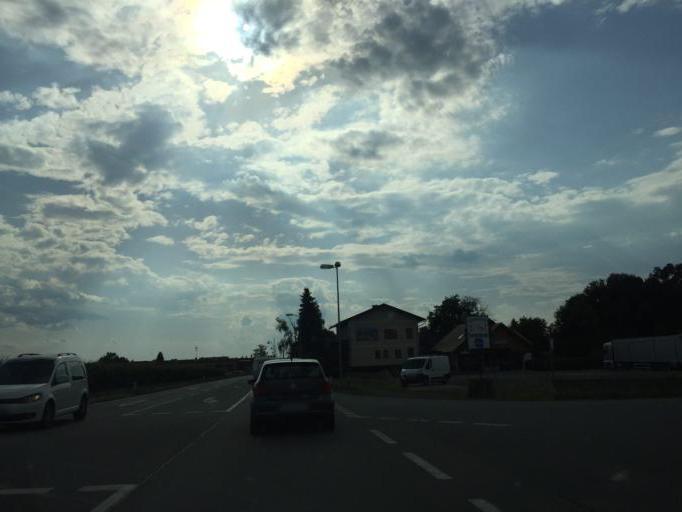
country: AT
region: Styria
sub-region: Politischer Bezirk Suedoststeiermark
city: Eichfeld
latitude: 46.7258
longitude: 15.7760
